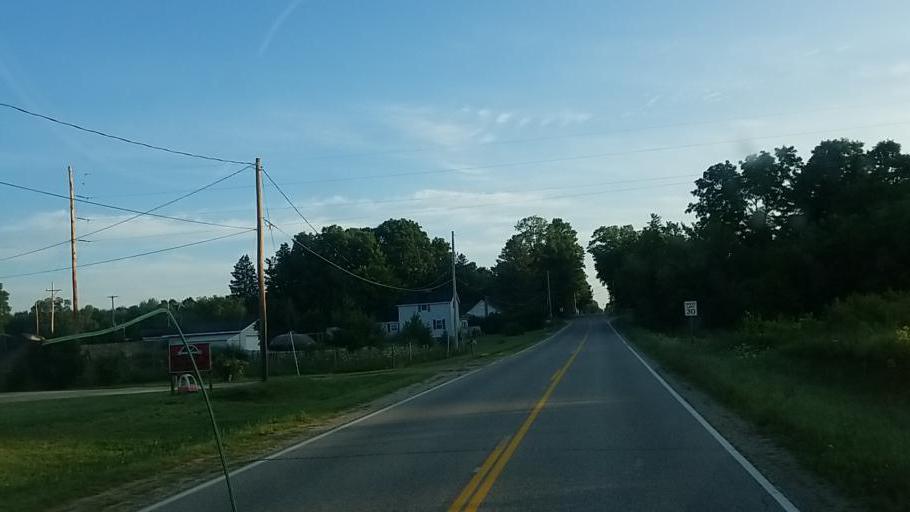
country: US
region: Michigan
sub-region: Montcalm County
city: Howard City
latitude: 43.3581
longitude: -85.4029
